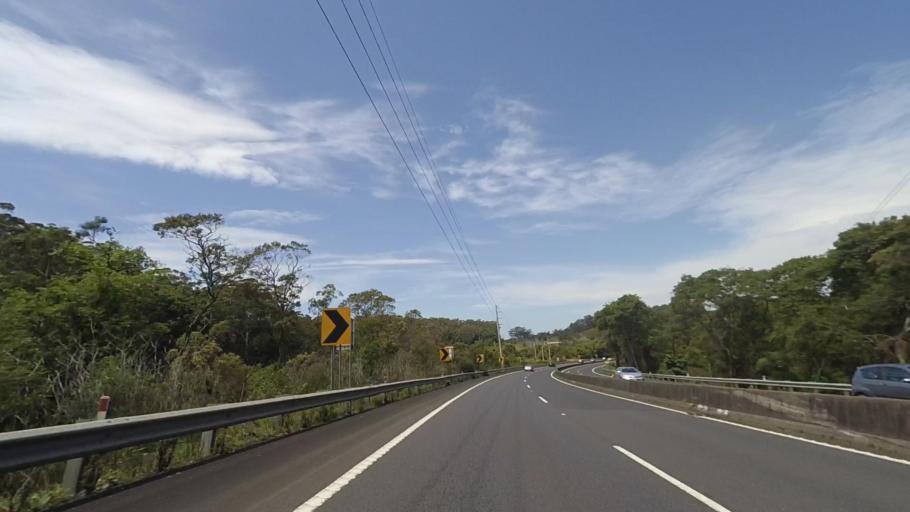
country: AU
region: New South Wales
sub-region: Wollongong
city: Bulli
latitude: -34.3350
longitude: 150.8805
